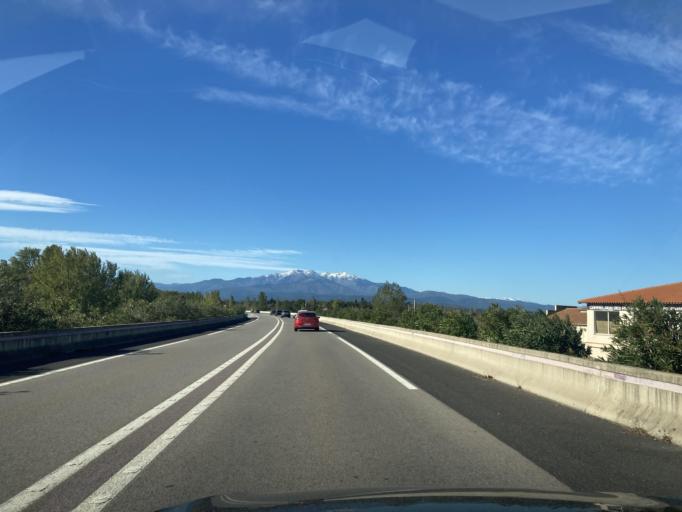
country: FR
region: Languedoc-Roussillon
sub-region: Departement des Pyrenees-Orientales
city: Sant Genis de Fontanes
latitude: 42.5483
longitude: 2.9174
